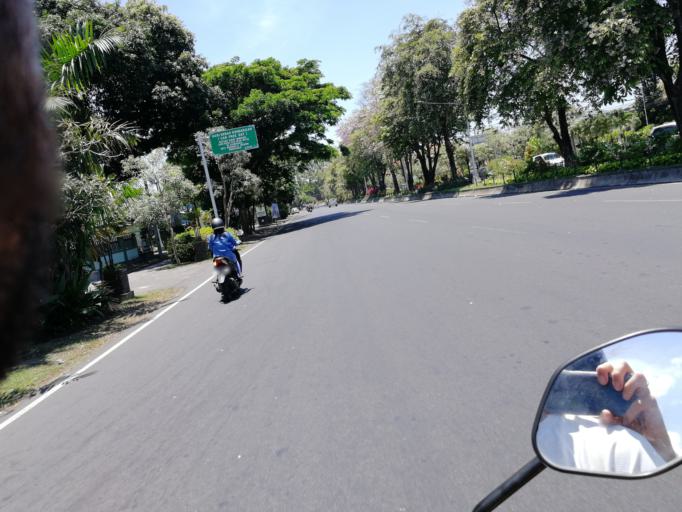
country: ID
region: Bali
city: Denpasar
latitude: -8.6696
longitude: 115.2185
